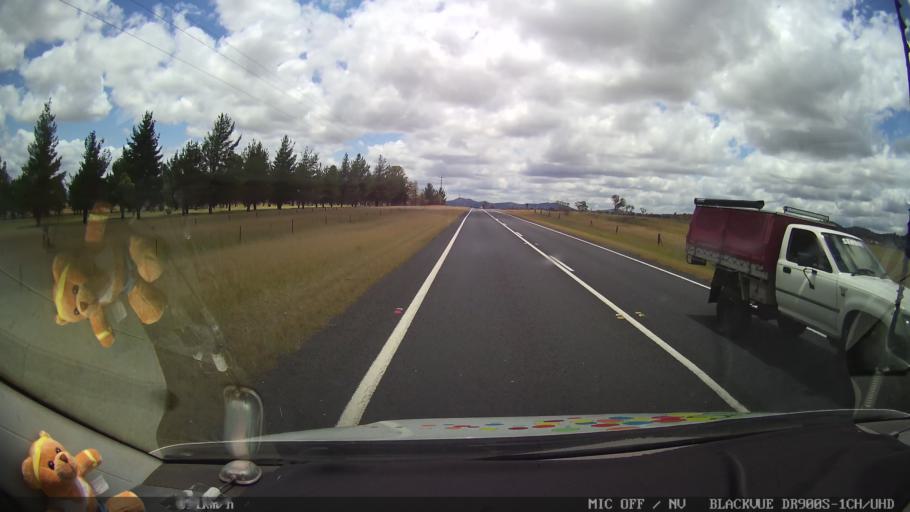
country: AU
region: New South Wales
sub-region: Glen Innes Severn
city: Glen Innes
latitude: -29.4301
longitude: 151.8555
